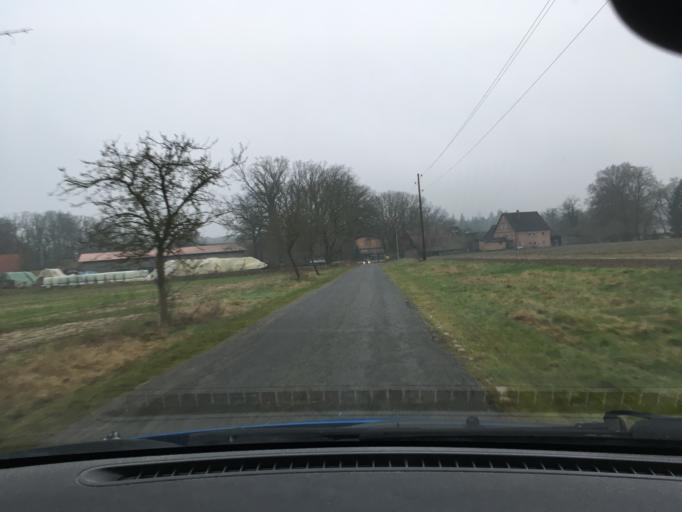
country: DE
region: Lower Saxony
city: Soderstorf
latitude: 53.0905
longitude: 10.1593
